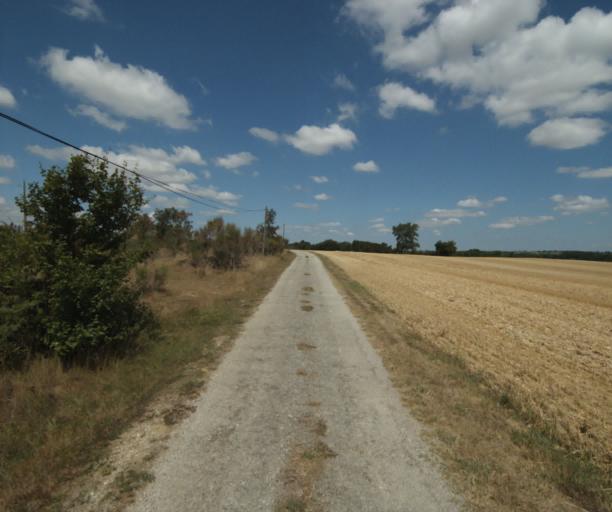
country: FR
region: Midi-Pyrenees
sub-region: Departement de la Haute-Garonne
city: Auriac-sur-Vendinelle
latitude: 43.4837
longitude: 1.8406
